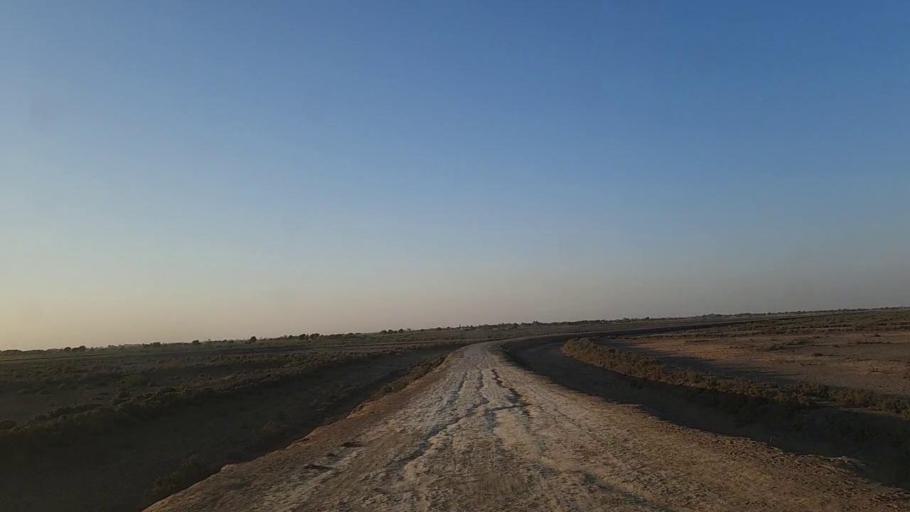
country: PK
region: Sindh
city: Naukot
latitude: 25.0069
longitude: 69.4179
